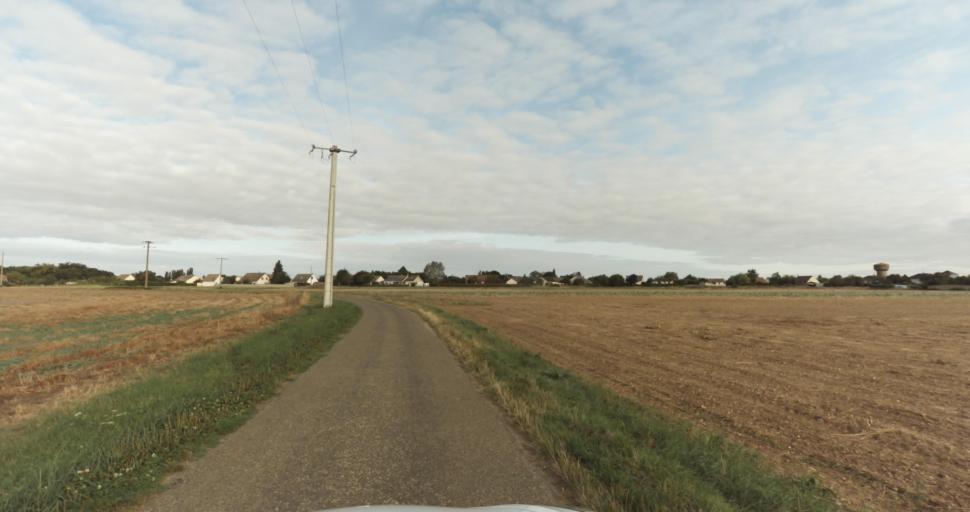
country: FR
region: Haute-Normandie
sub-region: Departement de l'Eure
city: Saint-Germain-sur-Avre
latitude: 48.8190
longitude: 1.2755
